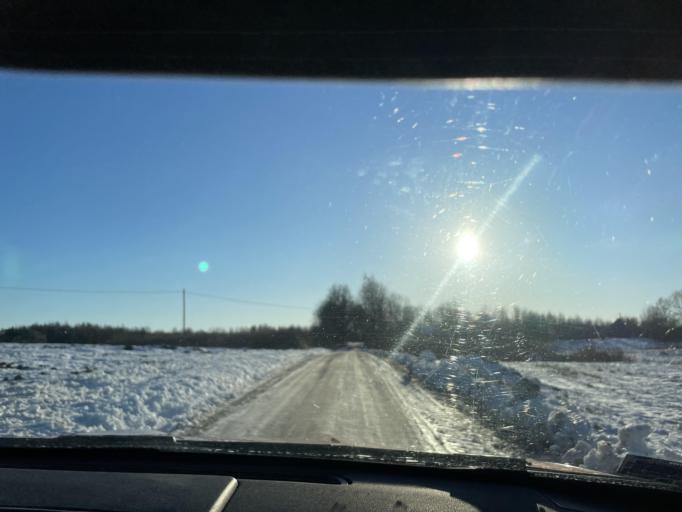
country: LV
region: Ludzas Rajons
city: Ludza
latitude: 56.4557
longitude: 27.6353
